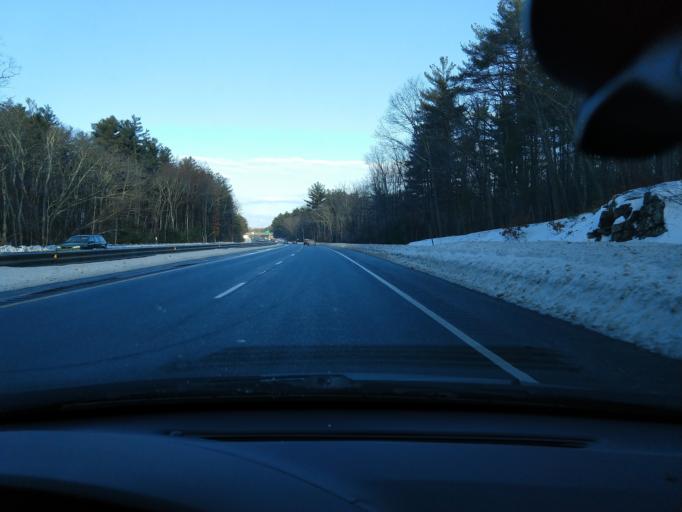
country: US
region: Massachusetts
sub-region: Middlesex County
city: Acton
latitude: 42.4858
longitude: -71.4540
